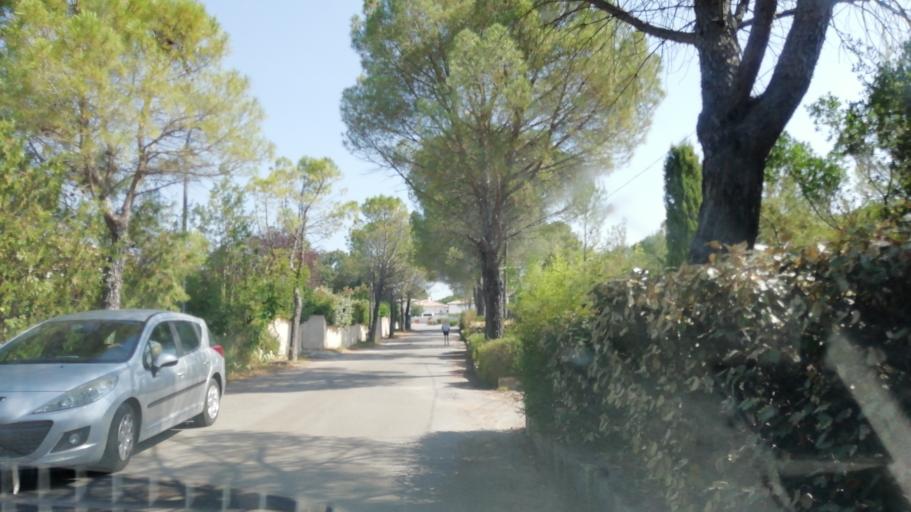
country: FR
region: Languedoc-Roussillon
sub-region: Departement de l'Herault
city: Saint-Mathieu-de-Treviers
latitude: 43.7418
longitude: 3.8568
